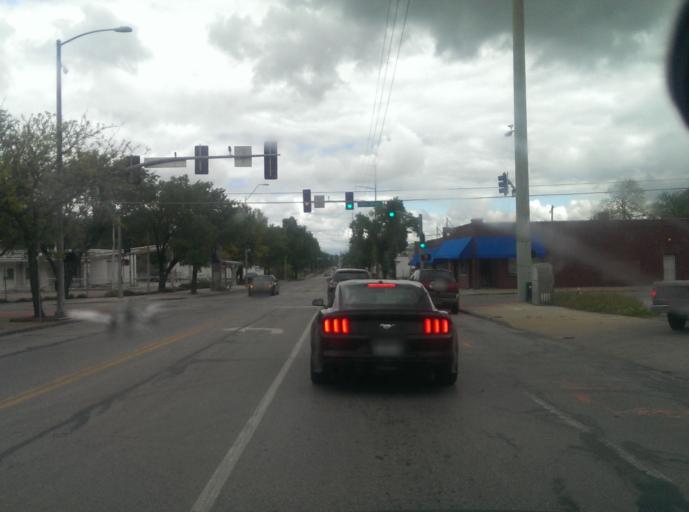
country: US
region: Kansas
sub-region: Johnson County
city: Mission Hills
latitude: 39.0268
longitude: -94.5738
